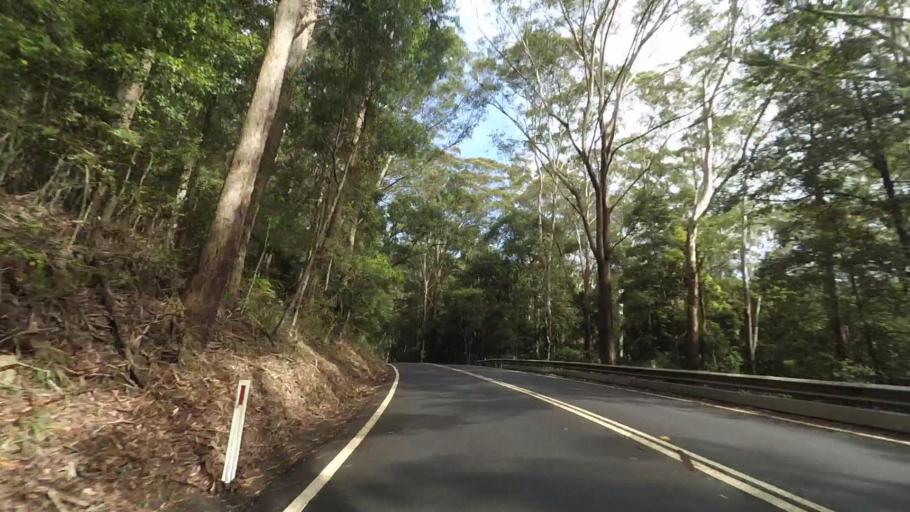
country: AU
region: New South Wales
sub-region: Wollongong
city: Helensburgh
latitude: -34.1991
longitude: 151.0101
